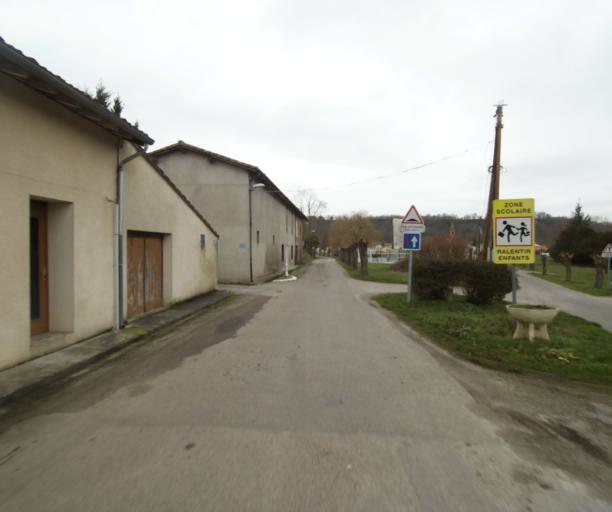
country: FR
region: Midi-Pyrenees
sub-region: Departement de l'Ariege
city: Saverdun
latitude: 43.1839
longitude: 1.6061
